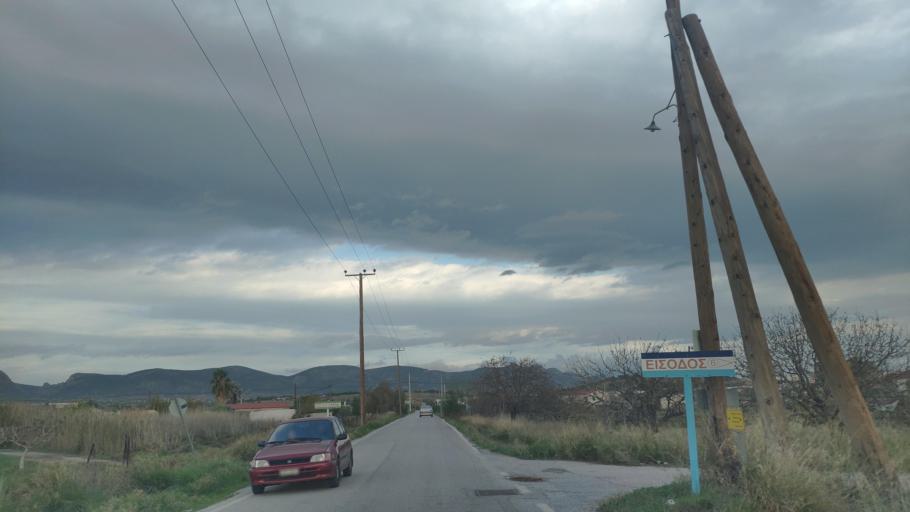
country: GR
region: Attica
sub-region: Nomarchia Dytikis Attikis
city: Nea Peramos
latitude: 37.9870
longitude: 23.3899
